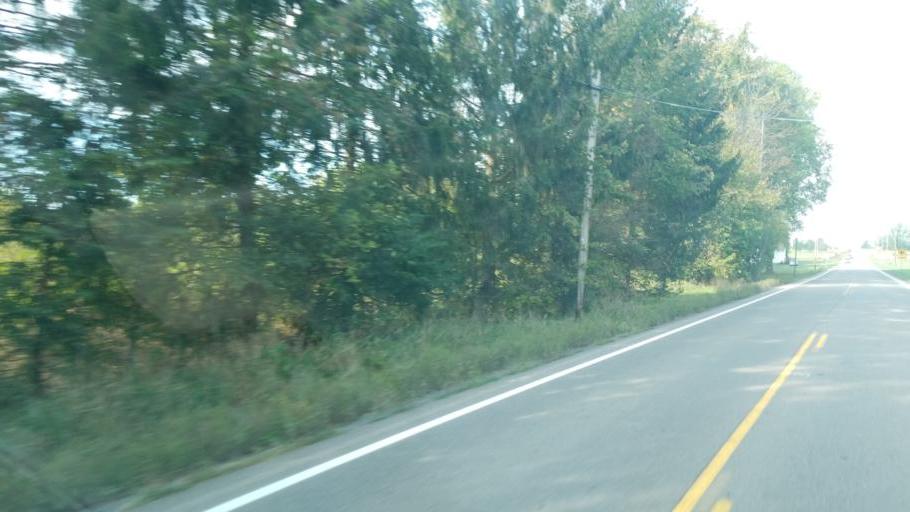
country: US
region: Ohio
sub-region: Knox County
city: Gambier
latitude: 40.3200
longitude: -82.3117
